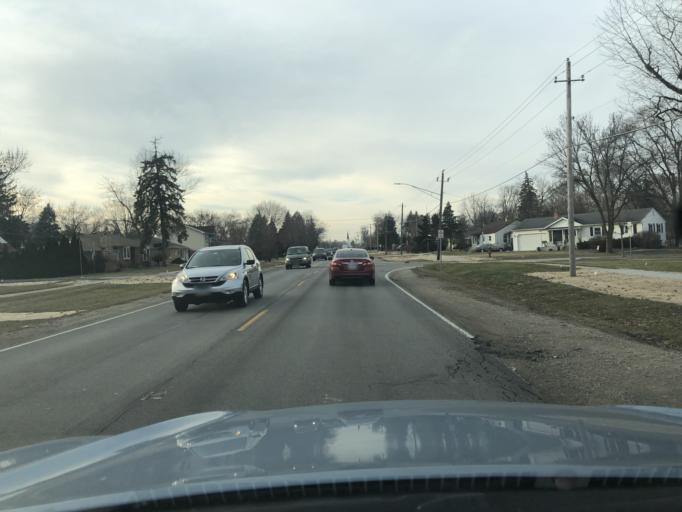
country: US
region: Illinois
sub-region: DuPage County
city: Itasca
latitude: 41.9675
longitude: -88.0038
